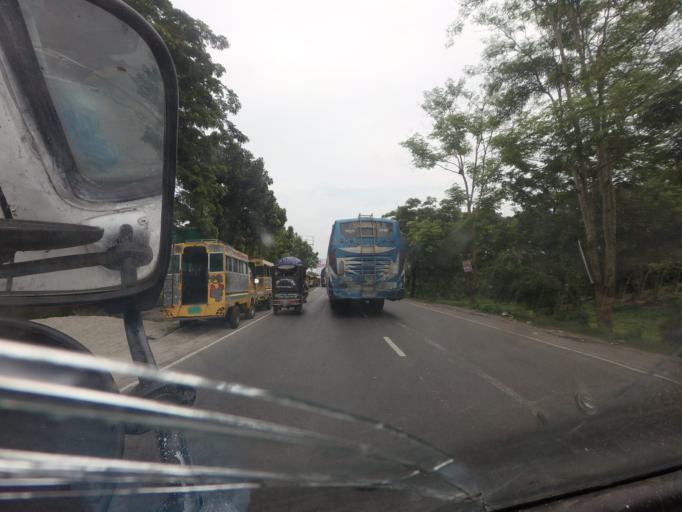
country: BD
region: Dhaka
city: Char Bhadrasan
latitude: 23.3904
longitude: 89.9828
